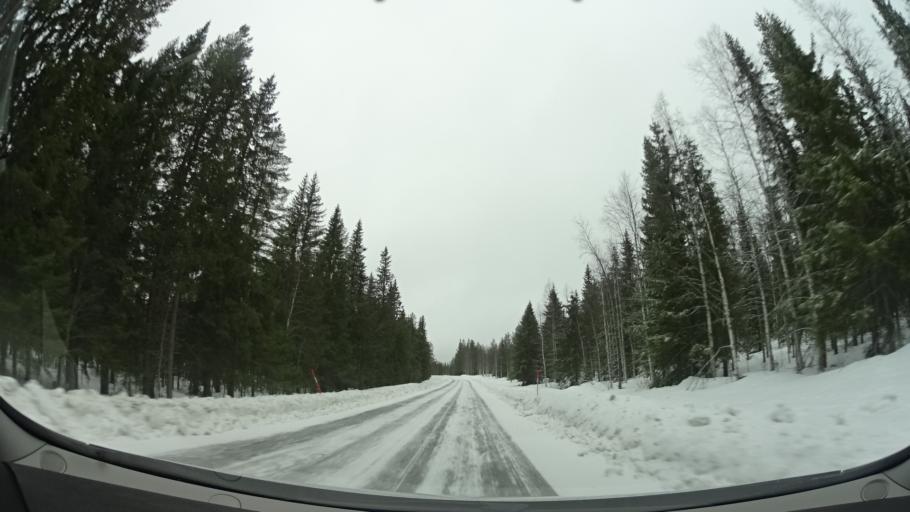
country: SE
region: Vaesterbotten
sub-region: Mala Kommun
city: Mala
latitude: 65.0973
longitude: 18.9203
